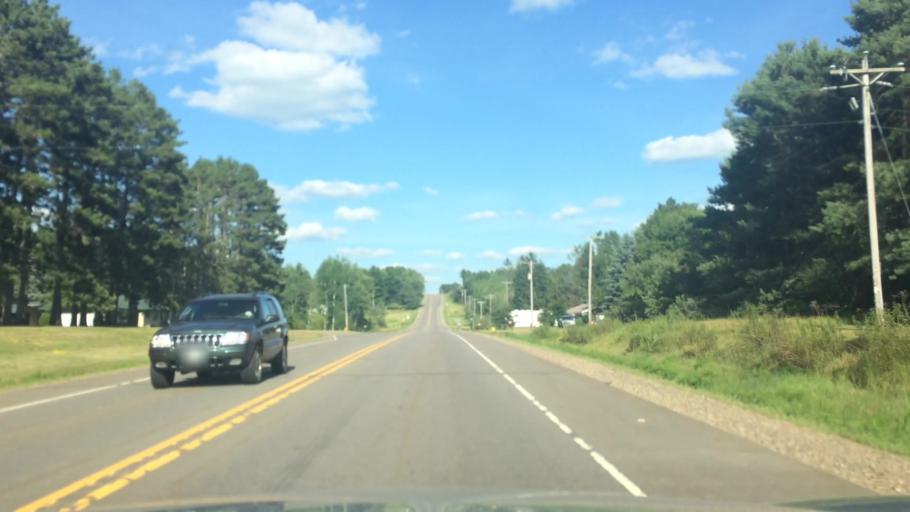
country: US
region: Wisconsin
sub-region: Lincoln County
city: Merrill
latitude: 45.1779
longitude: -89.6342
